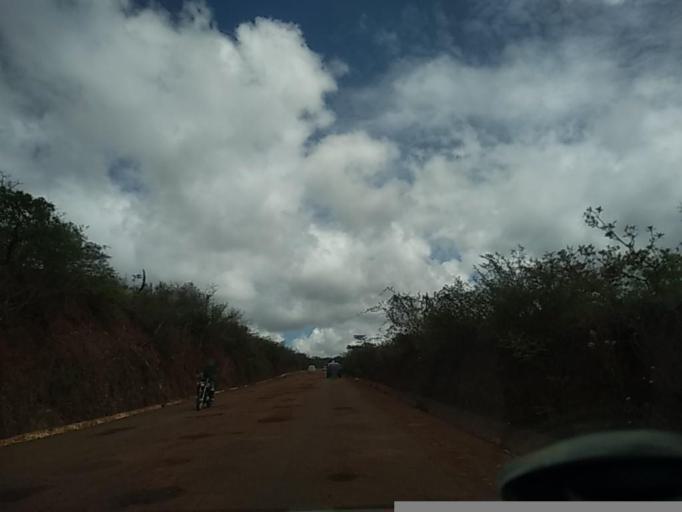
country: BR
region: Bahia
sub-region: Caetite
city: Caetite
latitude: -14.0301
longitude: -42.4874
